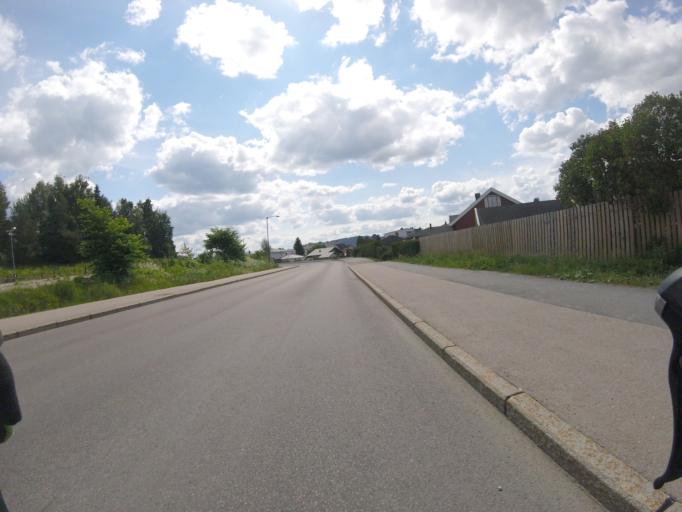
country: NO
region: Akershus
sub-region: Skedsmo
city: Lillestrom
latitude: 59.9733
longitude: 11.0484
